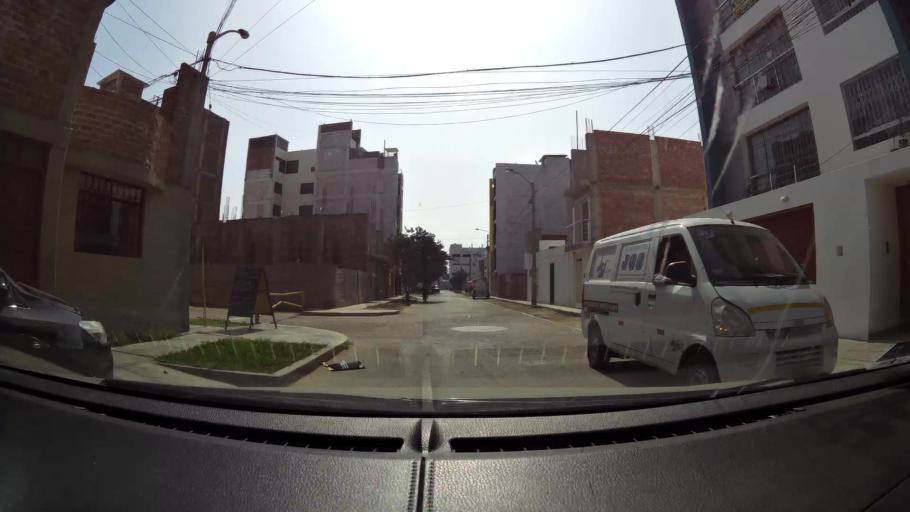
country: PE
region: La Libertad
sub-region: Provincia de Trujillo
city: Trujillo
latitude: -8.1279
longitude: -79.0286
